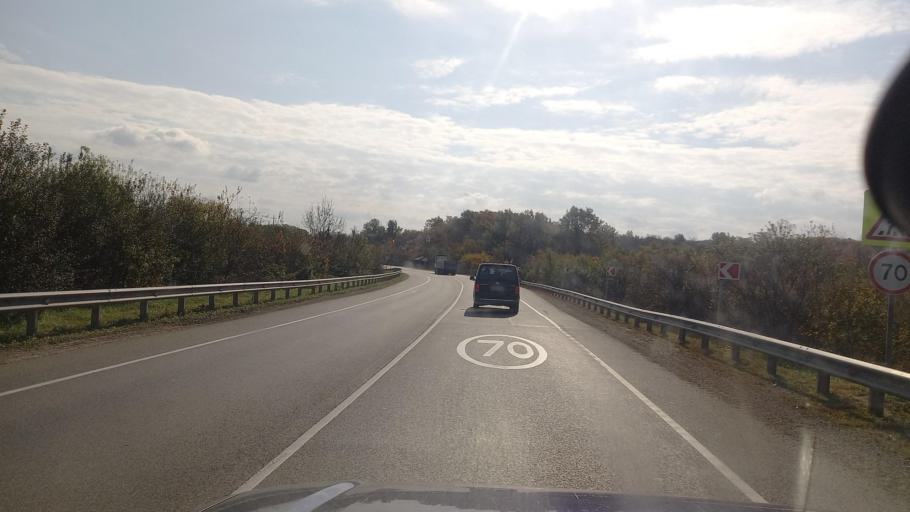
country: RU
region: Krasnodarskiy
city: Abinsk
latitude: 44.8512
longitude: 38.1353
